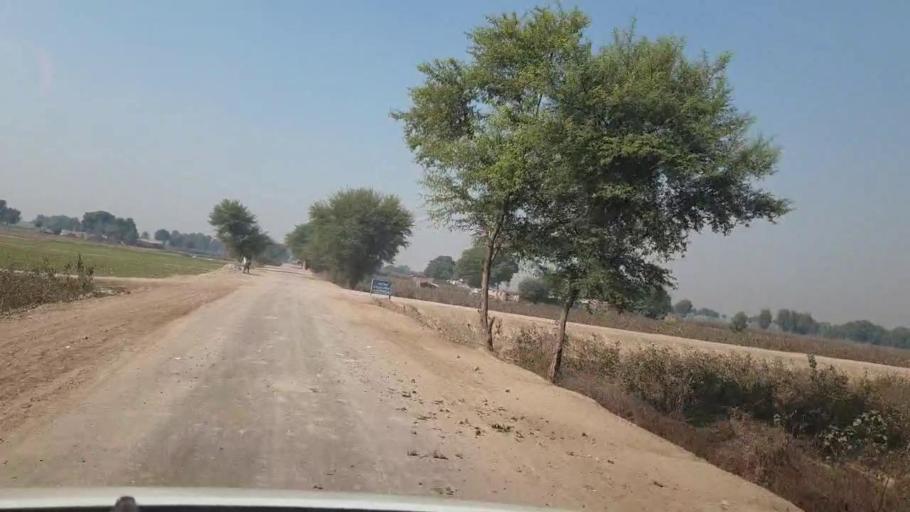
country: PK
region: Sindh
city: Bhan
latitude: 26.6117
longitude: 67.7693
